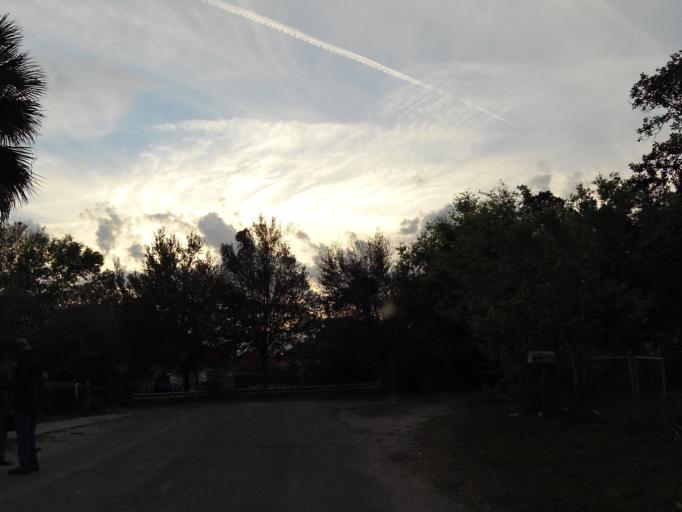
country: US
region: Florida
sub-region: Duval County
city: Jacksonville
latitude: 30.3597
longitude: -81.6347
